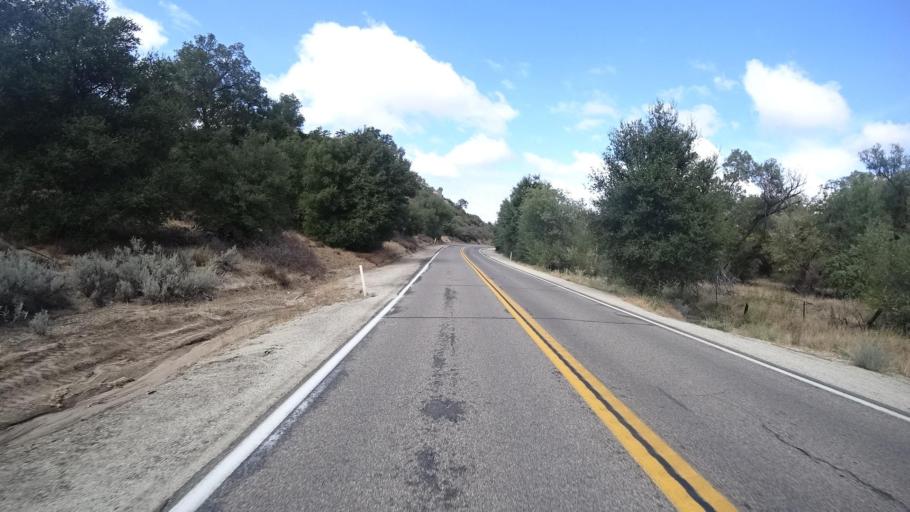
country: US
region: California
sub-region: San Diego County
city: Campo
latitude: 32.7022
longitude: -116.4896
